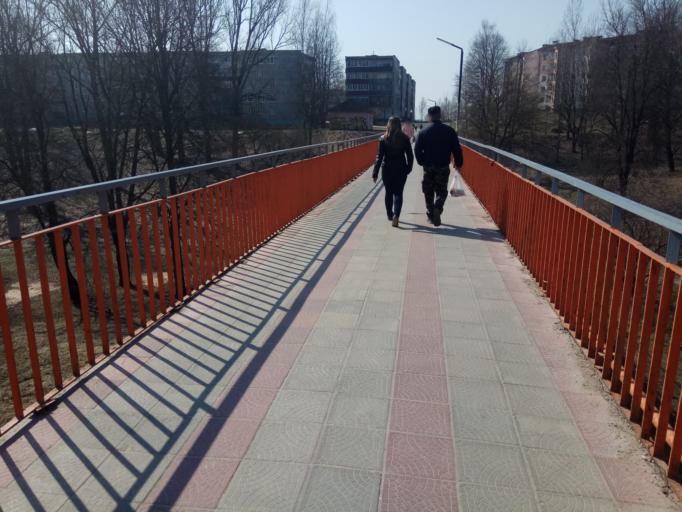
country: BY
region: Minsk
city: Valozhyn
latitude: 54.0882
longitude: 26.5217
